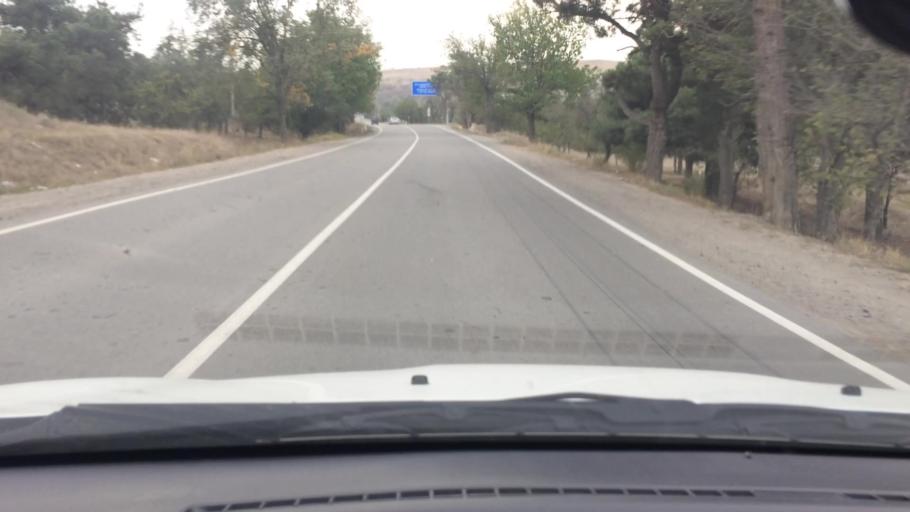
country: GE
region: Kvemo Kartli
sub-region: Gardabani
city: Gardabani
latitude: 41.3381
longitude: 45.0689
